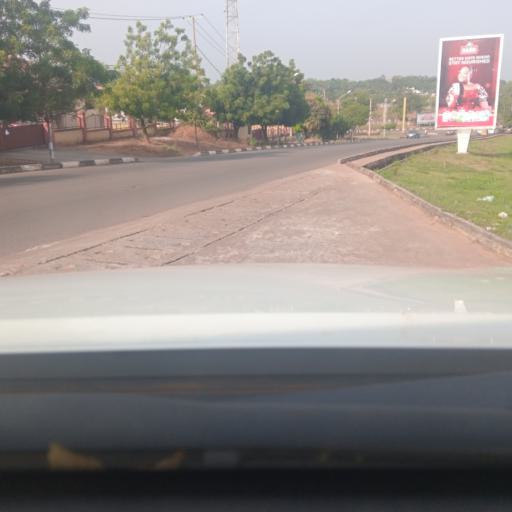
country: NG
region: Enugu
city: Enugu
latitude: 6.4381
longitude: 7.5155
